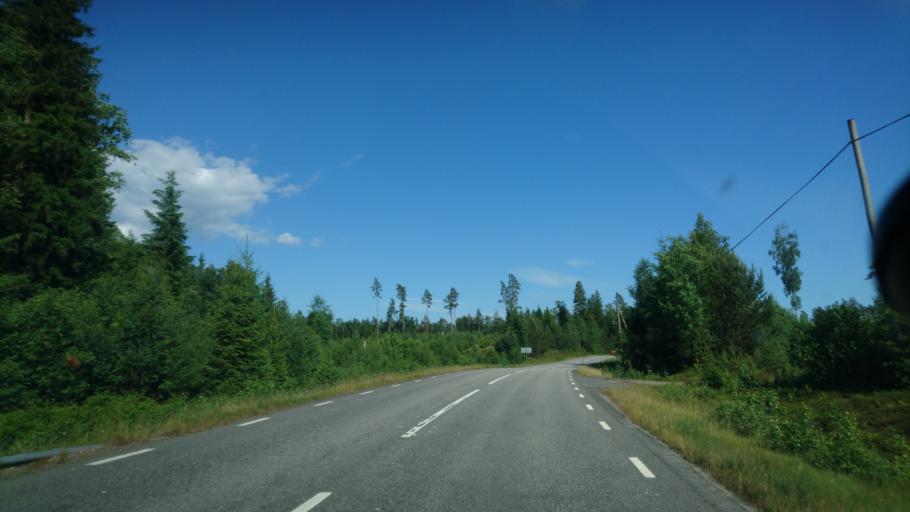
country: SE
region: Skane
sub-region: Osby Kommun
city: Lonsboda
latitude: 56.4148
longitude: 14.2973
